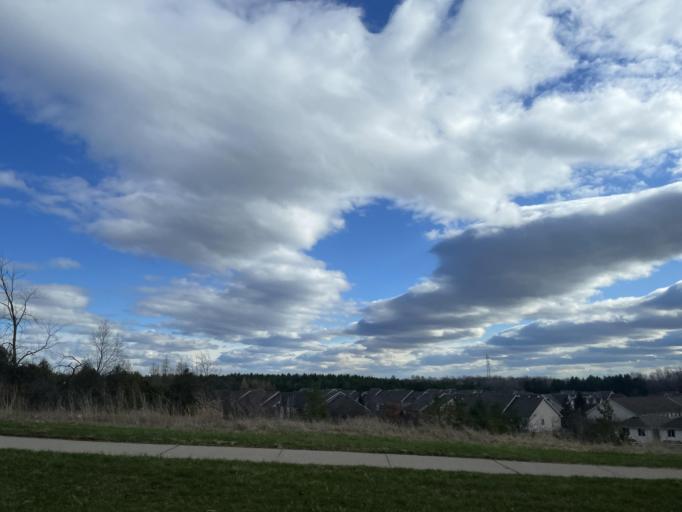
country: CA
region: Ontario
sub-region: Wellington County
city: Guelph
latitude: 43.5107
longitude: -80.2116
